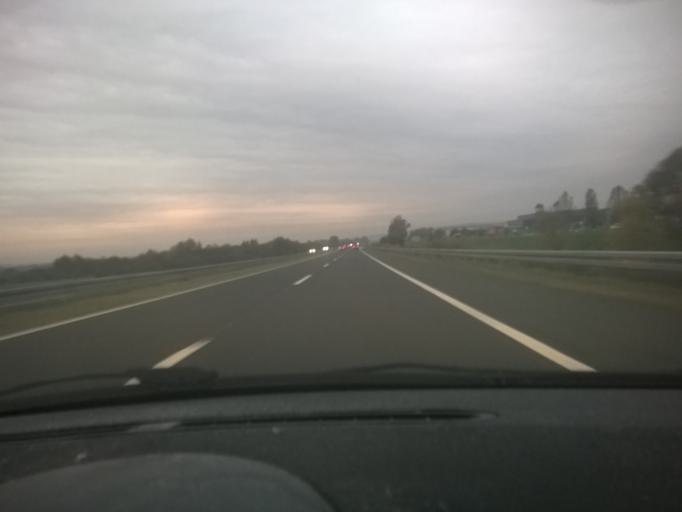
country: HR
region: Krapinsko-Zagorska
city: Zabok
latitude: 46.0215
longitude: 15.9077
